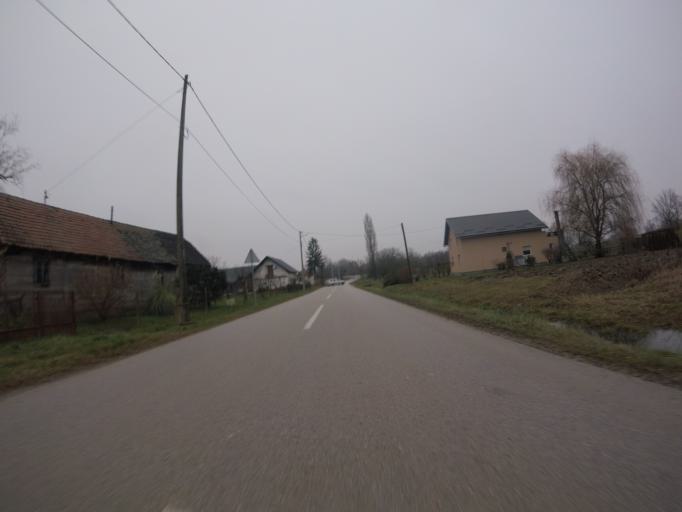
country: HR
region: Sisacko-Moslavacka
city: Lekenik
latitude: 45.6652
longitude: 16.2511
